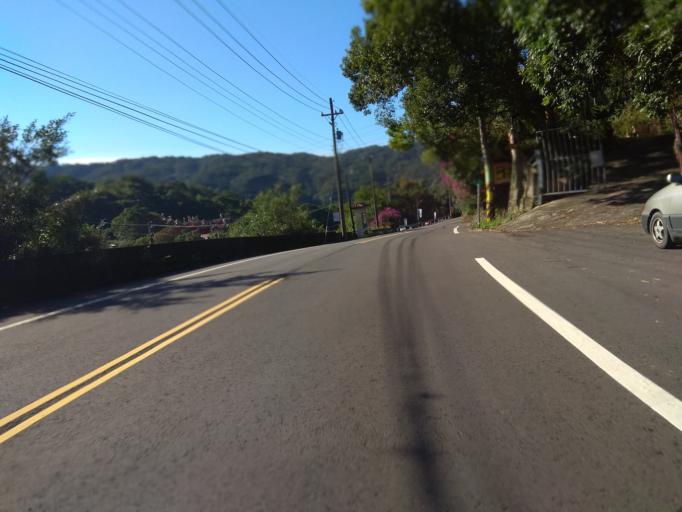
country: TW
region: Taiwan
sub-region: Hsinchu
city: Zhubei
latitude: 24.8495
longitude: 121.1454
